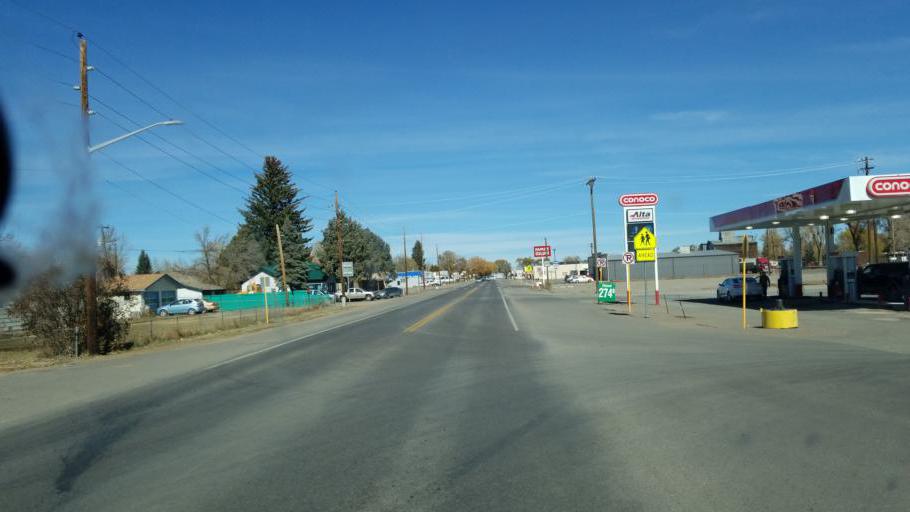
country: US
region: Colorado
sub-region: Conejos County
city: Conejos
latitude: 37.2740
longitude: -105.9621
